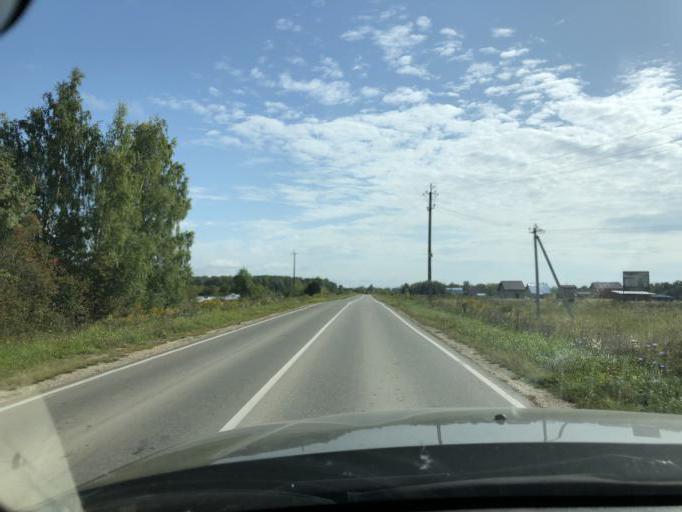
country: RU
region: Tula
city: Revyakino
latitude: 54.3656
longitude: 37.7058
